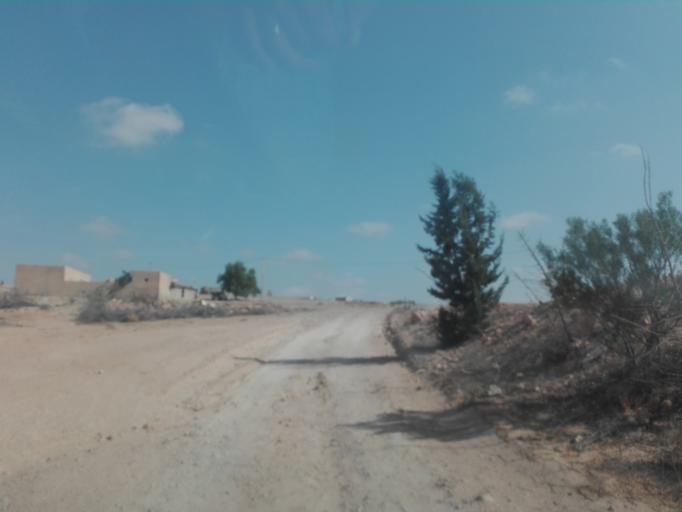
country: TN
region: Madanin
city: Medenine
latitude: 33.4387
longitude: 10.4318
